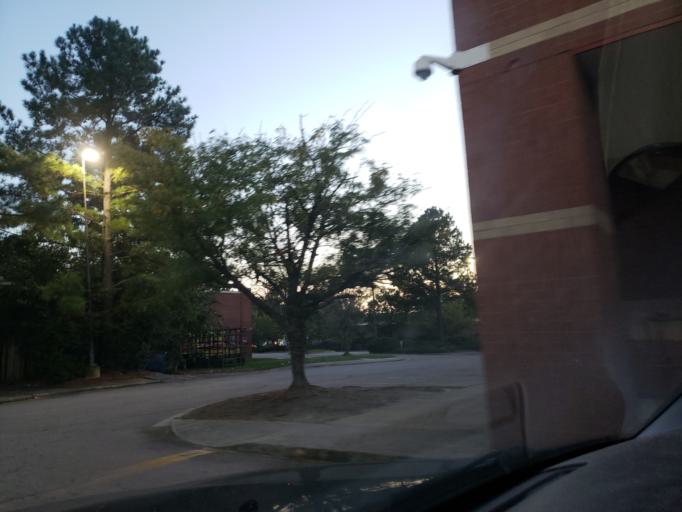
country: US
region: North Carolina
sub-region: Wake County
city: Raleigh
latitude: 35.7999
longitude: -78.5663
